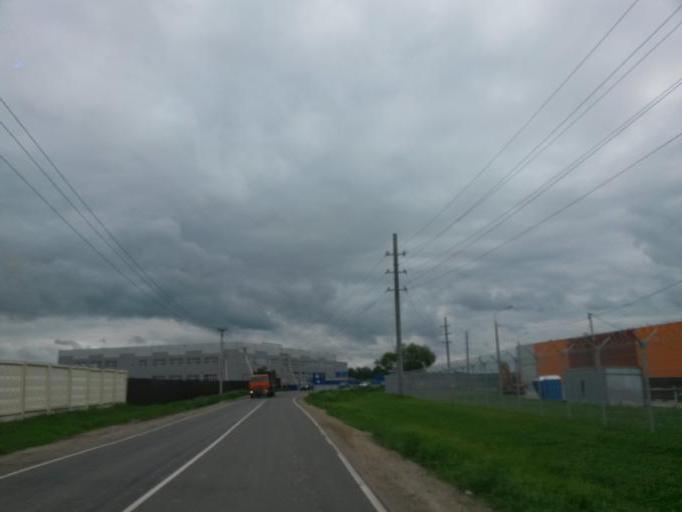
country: RU
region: Moskovskaya
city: Klimovsk
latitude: 55.3412
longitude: 37.5967
